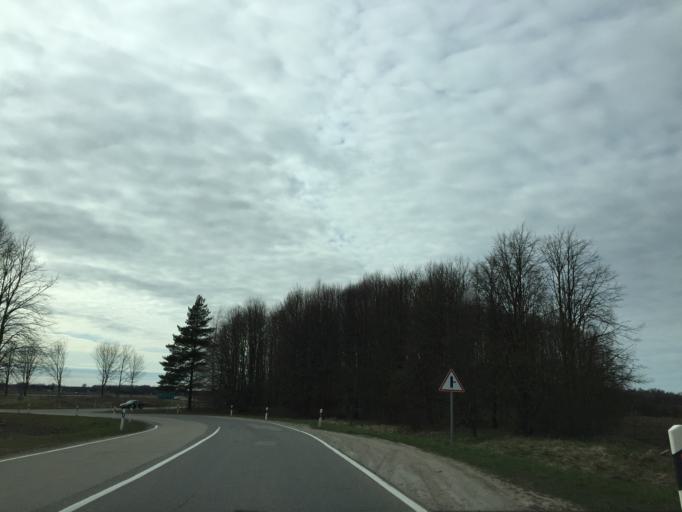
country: LT
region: Klaipedos apskritis
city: Gargzdai
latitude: 55.7169
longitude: 21.4513
